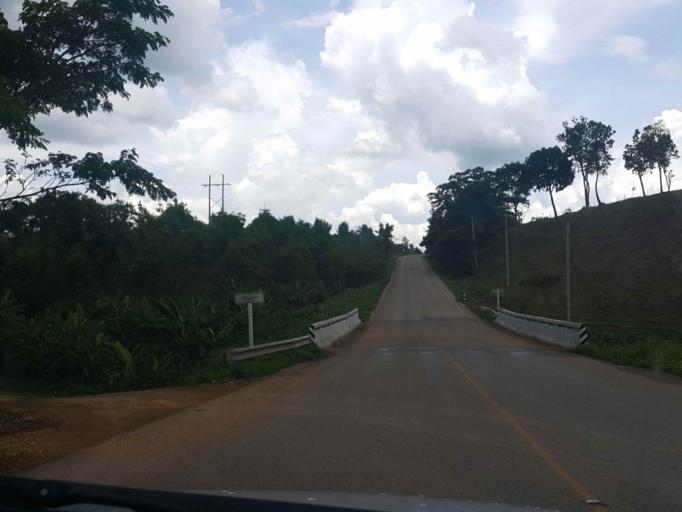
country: TH
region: Lampang
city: Ngao
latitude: 18.9412
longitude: 100.0769
